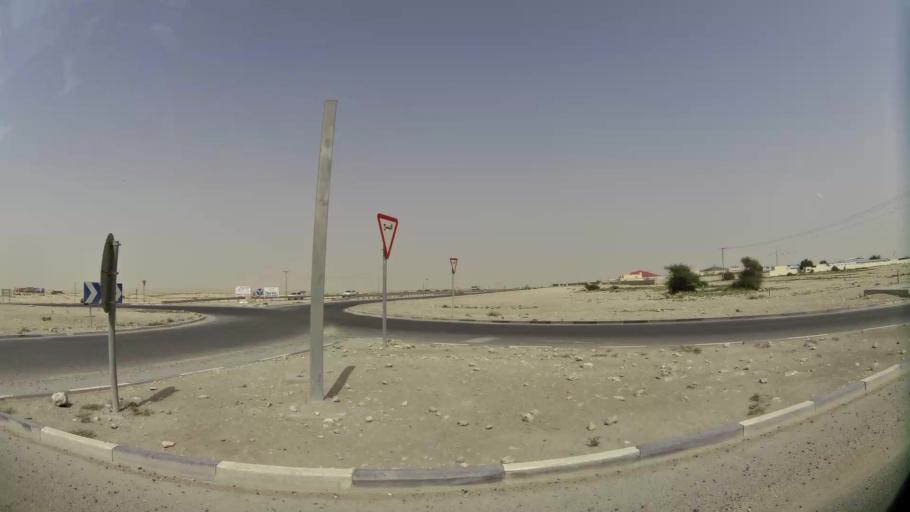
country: QA
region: Baladiyat ar Rayyan
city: Ar Rayyan
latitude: 25.2174
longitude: 51.3555
